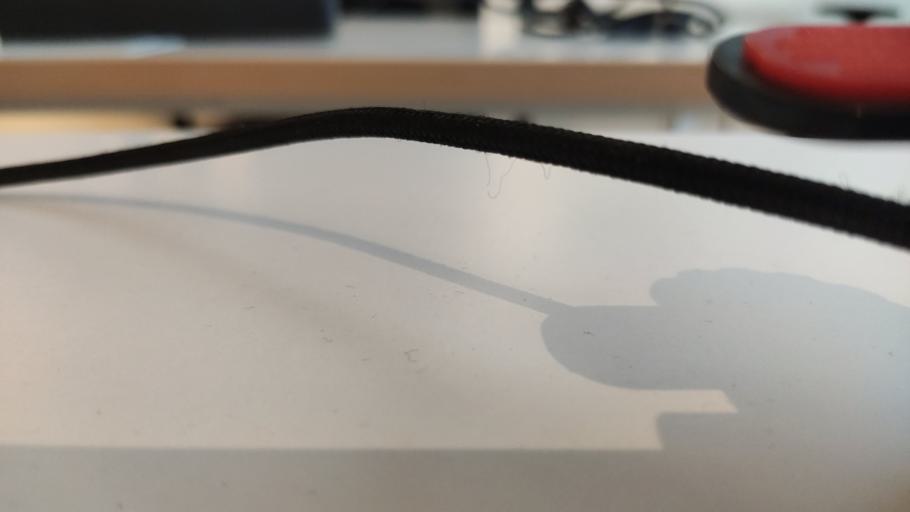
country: RU
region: Moskovskaya
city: Novopetrovskoye
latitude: 55.9710
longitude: 36.4416
